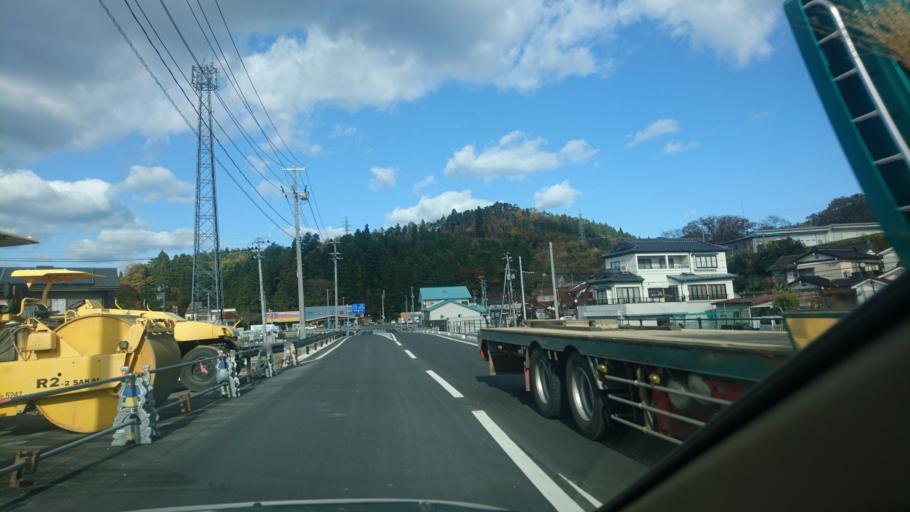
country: JP
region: Iwate
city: Ofunato
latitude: 38.9192
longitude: 141.5869
